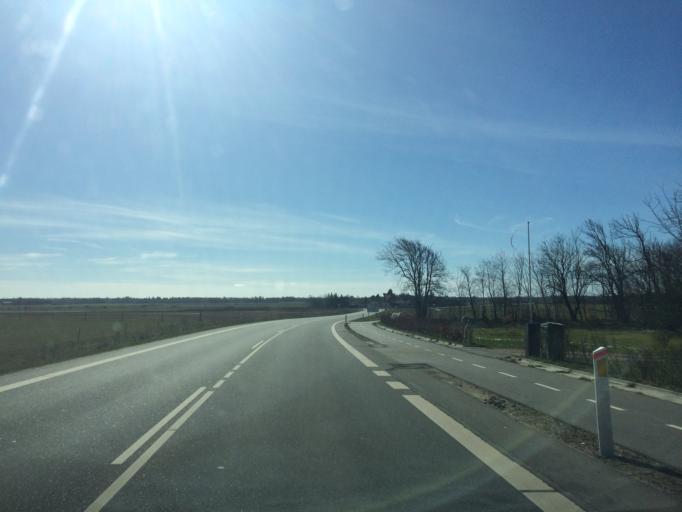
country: DK
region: Central Jutland
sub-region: Holstebro Kommune
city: Ulfborg
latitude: 56.2935
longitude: 8.3388
